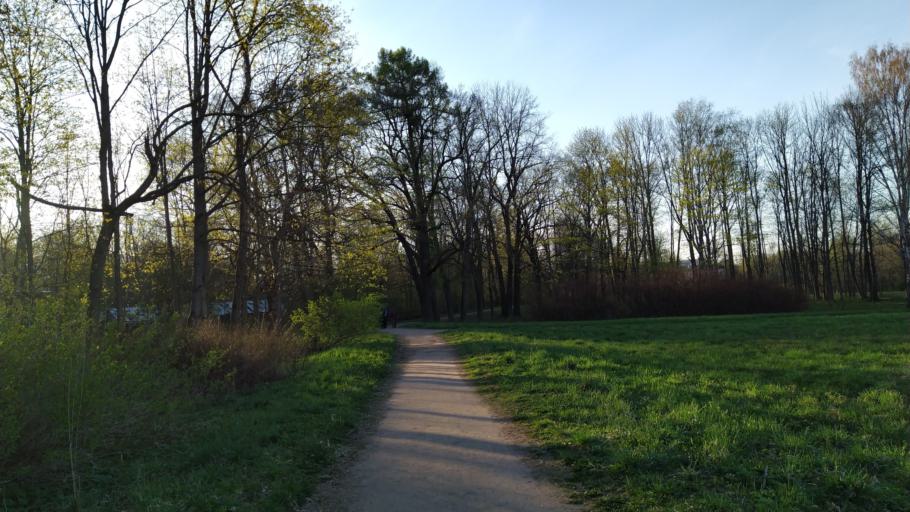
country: RU
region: St.-Petersburg
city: Pushkin
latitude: 59.7090
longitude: 30.4191
